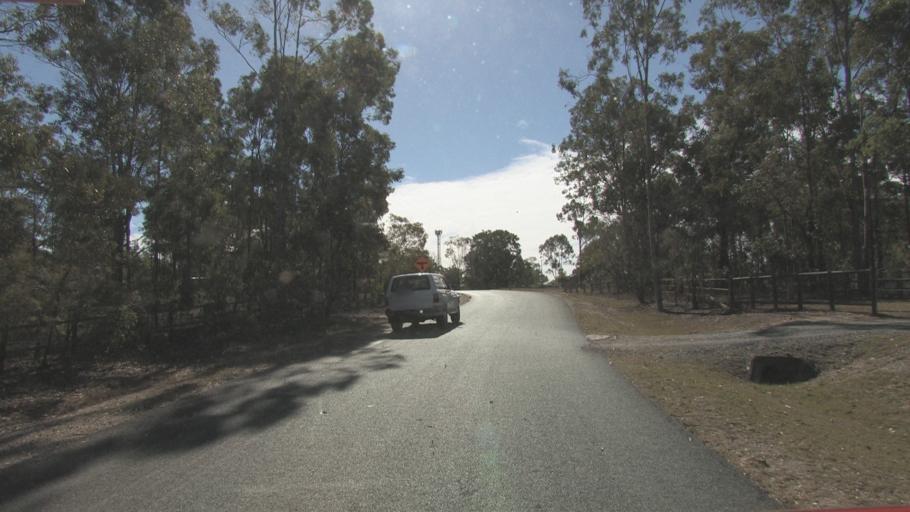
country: AU
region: Queensland
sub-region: Ipswich
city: Springfield Lakes
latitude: -27.7120
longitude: 152.9323
